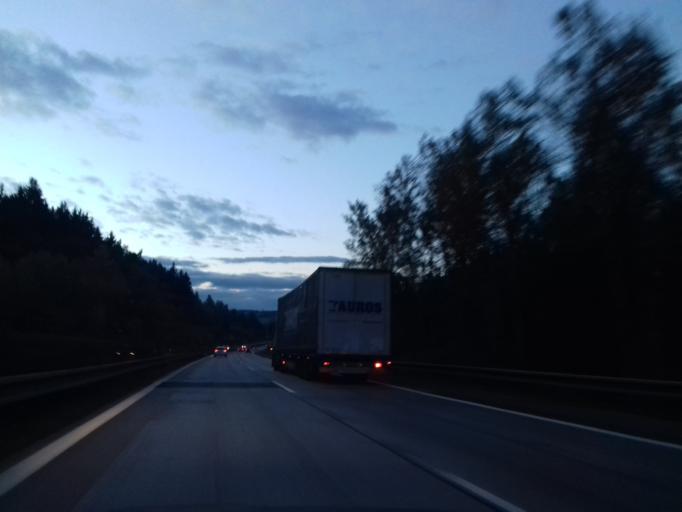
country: CZ
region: Central Bohemia
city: Divisov
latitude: 49.8117
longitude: 14.8833
